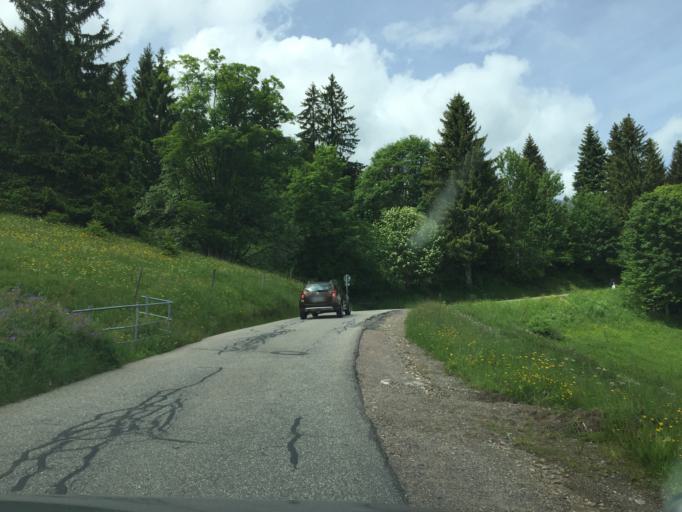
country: DE
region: Baden-Wuerttemberg
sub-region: Freiburg Region
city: Todtnau
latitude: 47.8558
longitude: 7.9398
